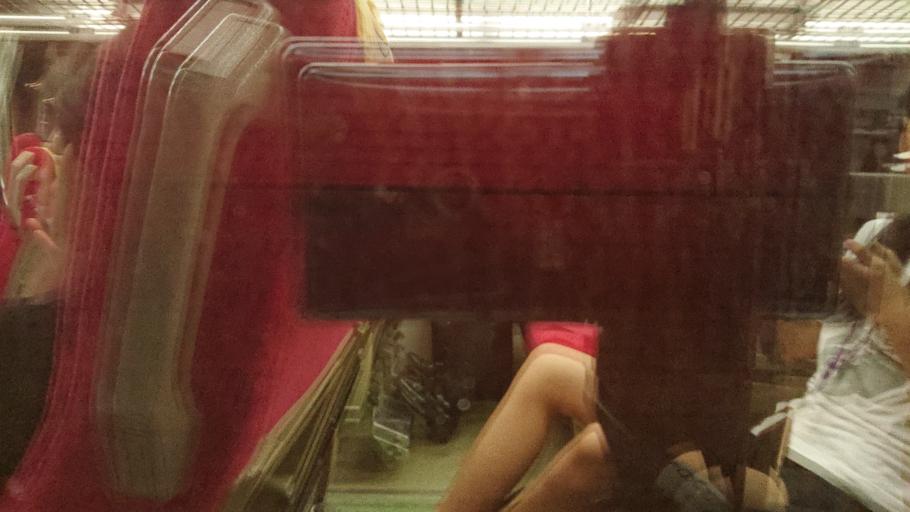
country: TW
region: Taiwan
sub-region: Keelung
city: Keelung
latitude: 24.9553
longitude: 121.9161
